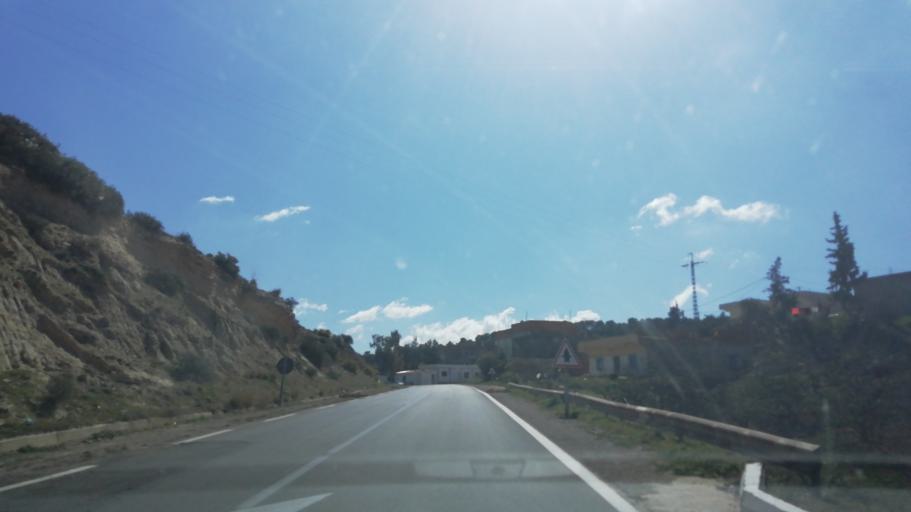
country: DZ
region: Mascara
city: Mascara
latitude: 35.4601
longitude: 0.1485
